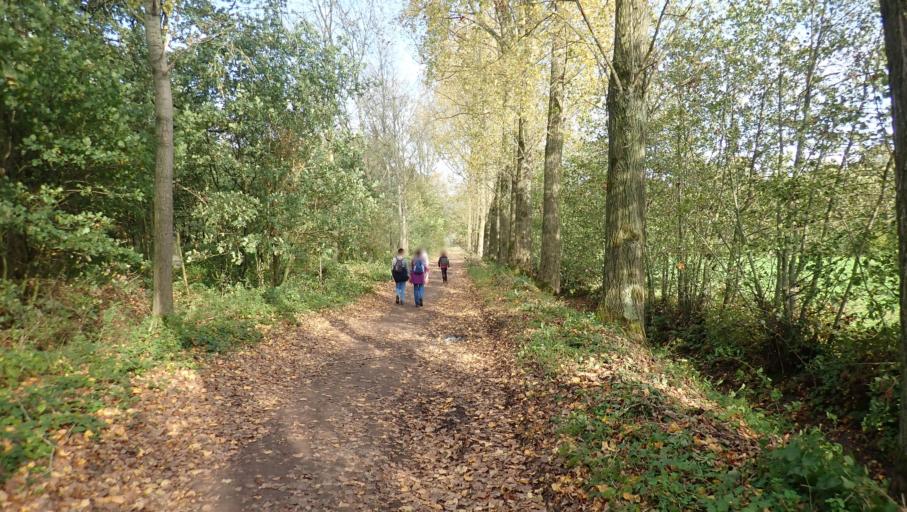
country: BE
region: Flanders
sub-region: Provincie Oost-Vlaanderen
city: Stekene
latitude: 51.1779
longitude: 4.0251
